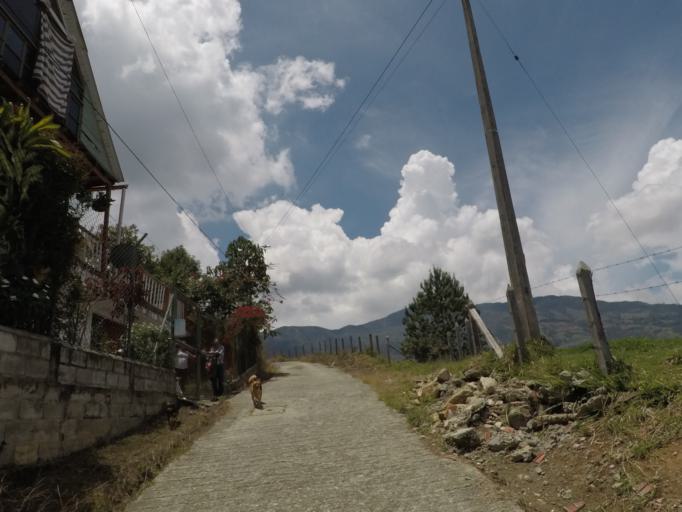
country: CO
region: Antioquia
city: Medellin
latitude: 6.2707
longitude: -75.6382
